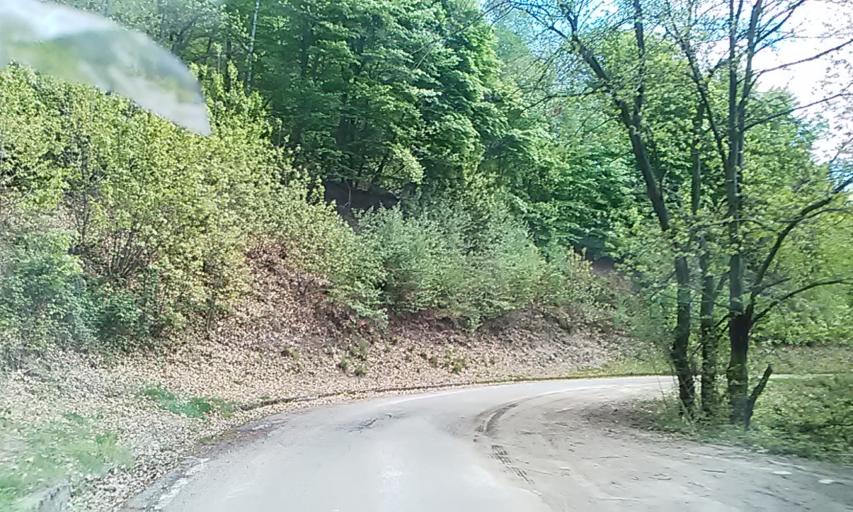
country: IT
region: Piedmont
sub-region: Provincia di Vercelli
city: Breia
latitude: 45.7761
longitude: 8.2950
